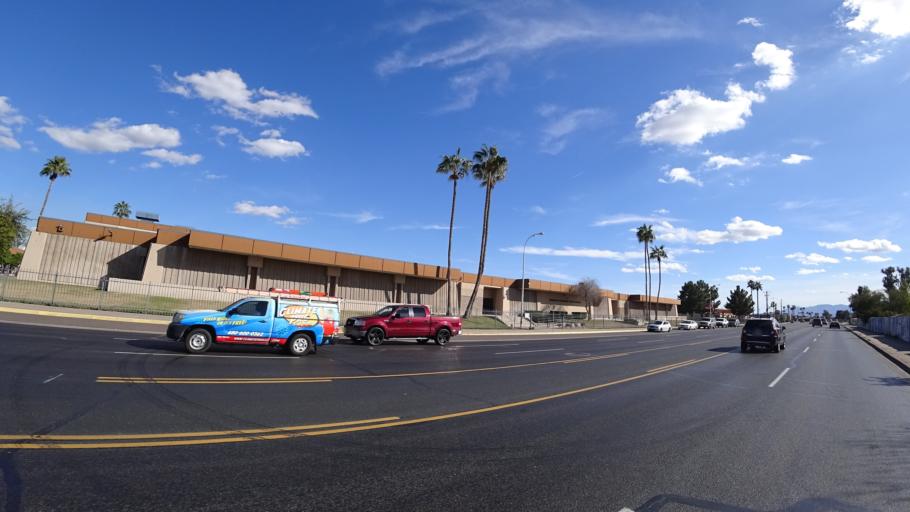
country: US
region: Arizona
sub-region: Maricopa County
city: Tolleson
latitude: 33.4836
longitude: -112.2207
